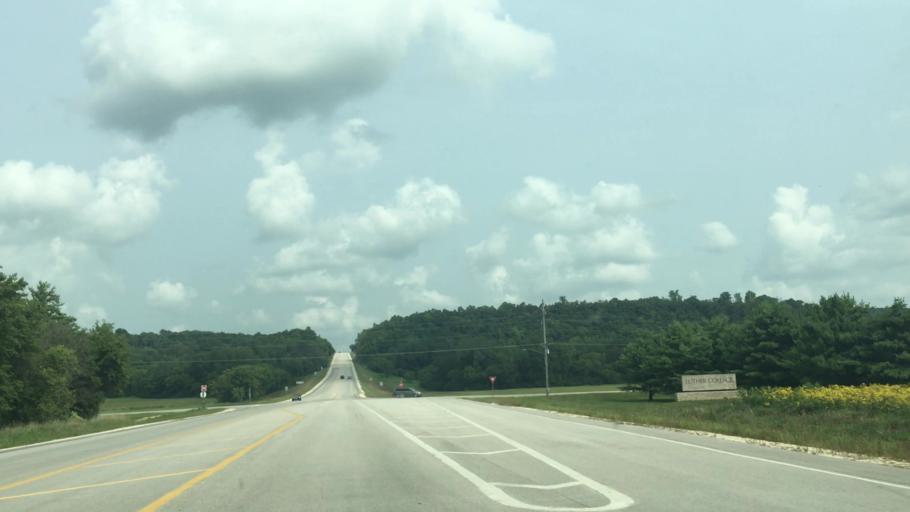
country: US
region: Iowa
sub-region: Winneshiek County
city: Decorah
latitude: 43.3191
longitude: -91.8140
